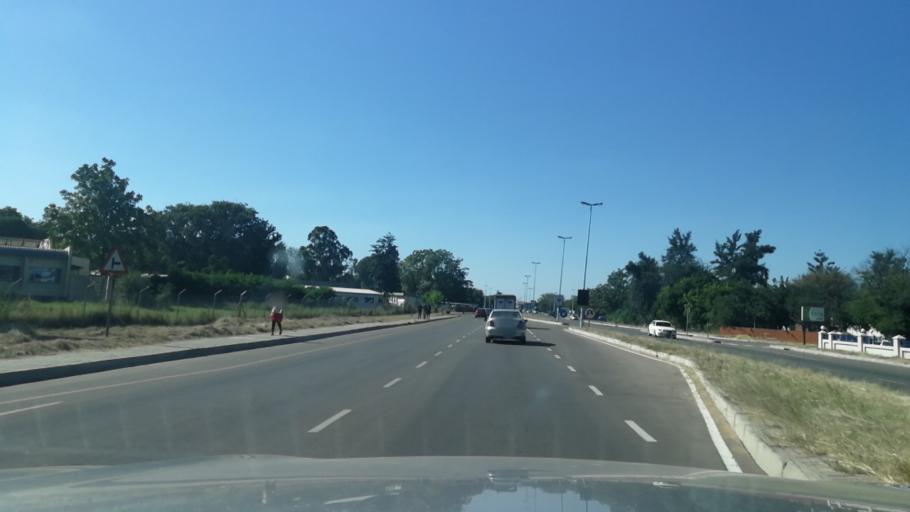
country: BW
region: South East
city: Gaborone
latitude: -24.6752
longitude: 25.9218
